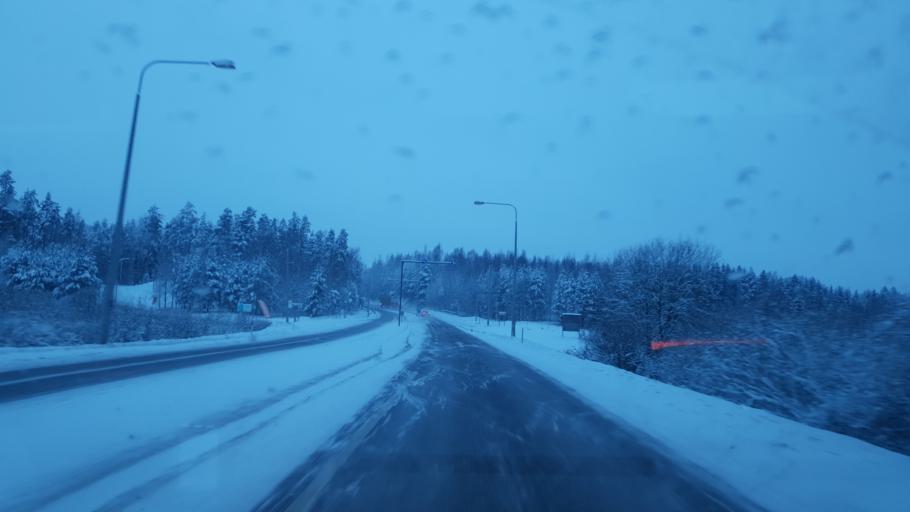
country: FI
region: Uusimaa
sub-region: Helsinki
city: Kerava
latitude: 60.3855
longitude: 25.1471
